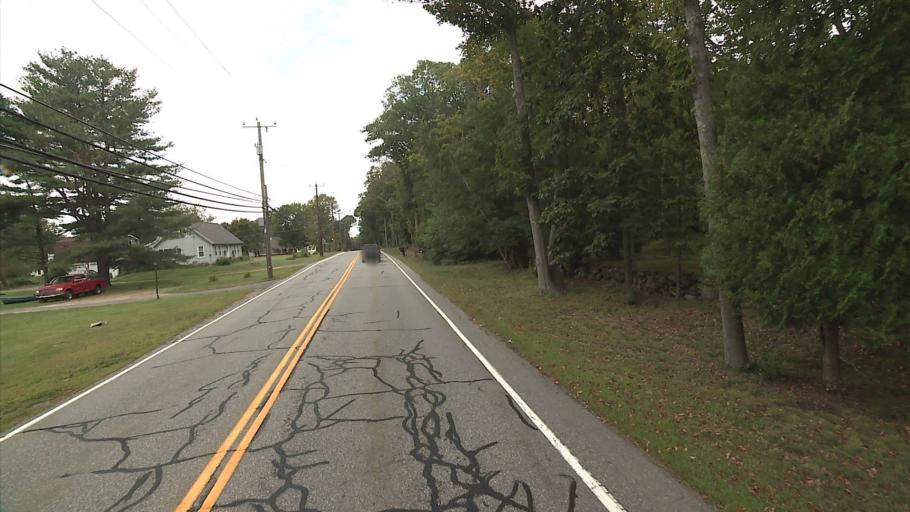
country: US
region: Connecticut
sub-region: Tolland County
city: Storrs
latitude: 41.8329
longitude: -72.2687
